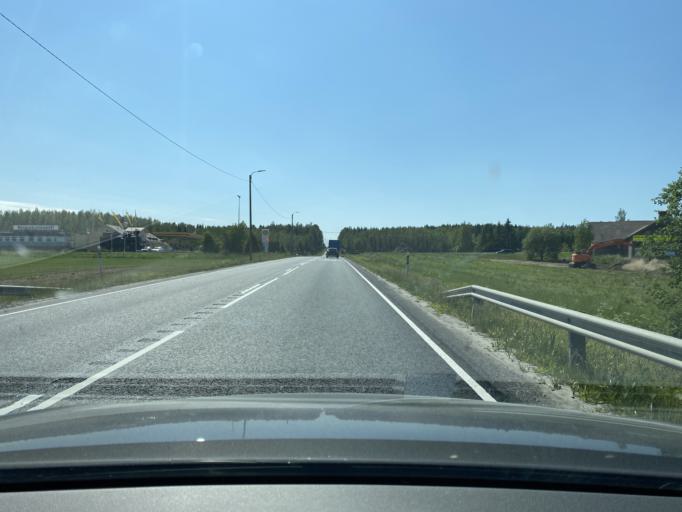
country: FI
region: Pirkanmaa
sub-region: Lounais-Pirkanmaa
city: Mouhijaervi
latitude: 61.3601
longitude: 23.0931
